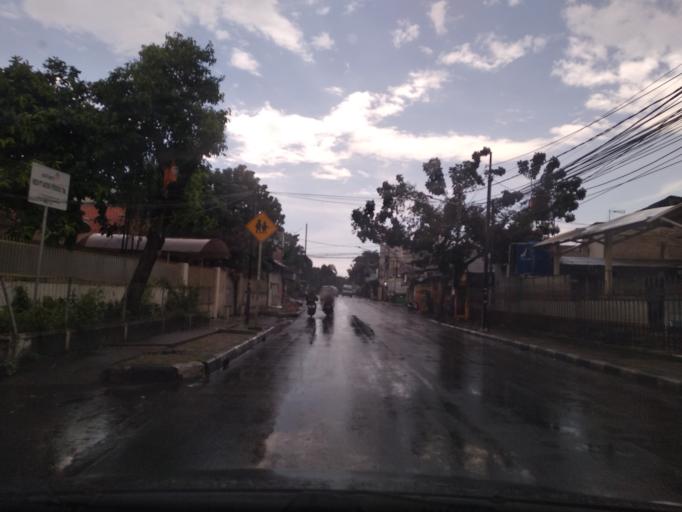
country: ID
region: Jakarta Raya
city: Jakarta
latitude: -6.2168
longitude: 106.8870
